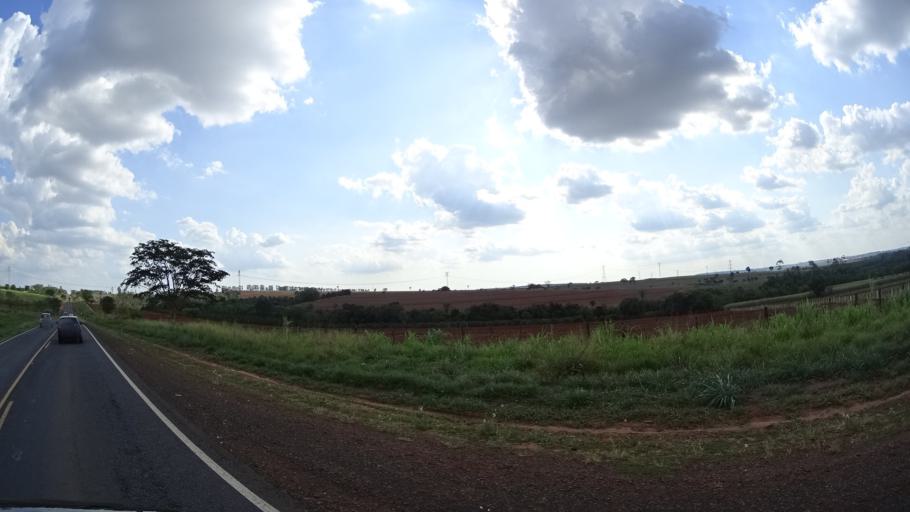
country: BR
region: Sao Paulo
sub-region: Urupes
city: Urupes
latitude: -21.1400
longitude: -49.2798
